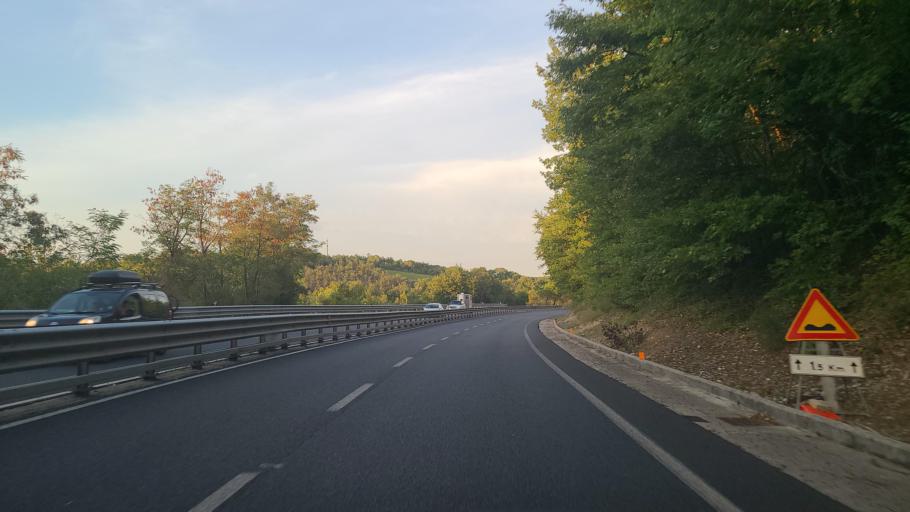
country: IT
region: Tuscany
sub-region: Province of Florence
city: Barberino Val d'Elsa
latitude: 43.5302
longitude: 11.2098
